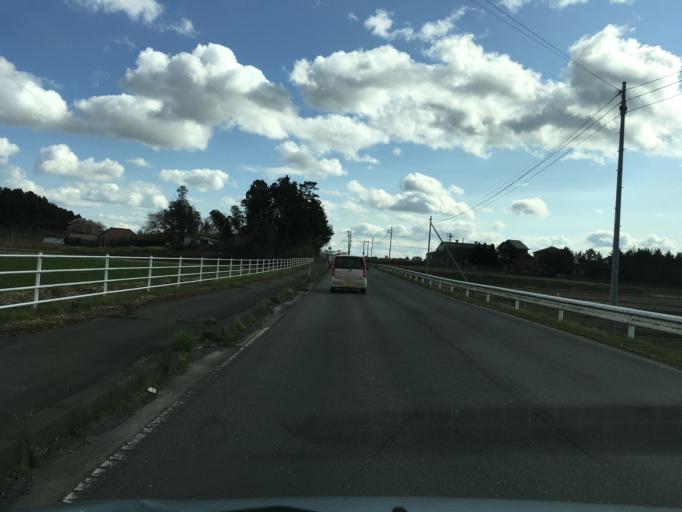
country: JP
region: Miyagi
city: Wakuya
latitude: 38.6549
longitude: 141.1923
